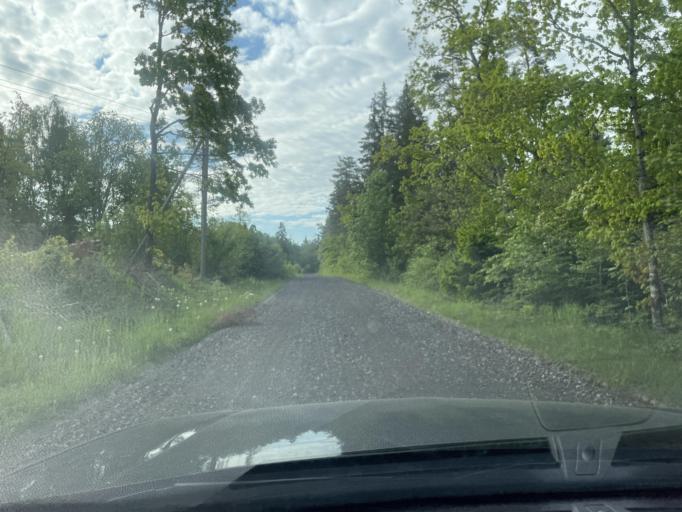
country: EE
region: Harju
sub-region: Keila linn
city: Keila
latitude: 59.3055
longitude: 24.2972
